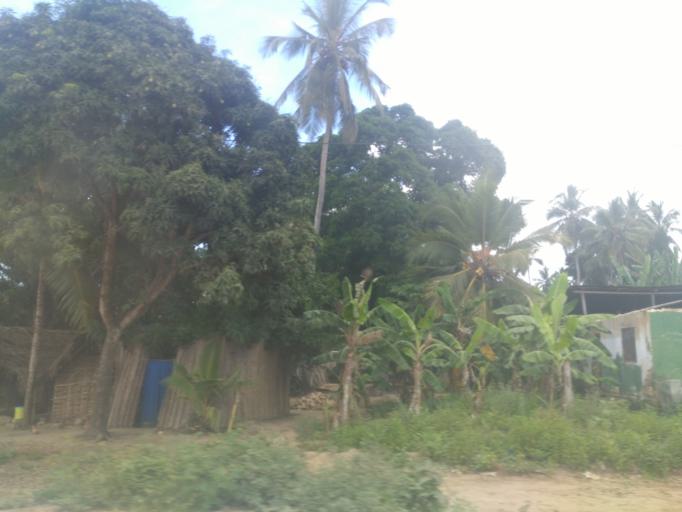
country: TZ
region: Zanzibar North
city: Gamba
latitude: -5.9734
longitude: 39.3012
